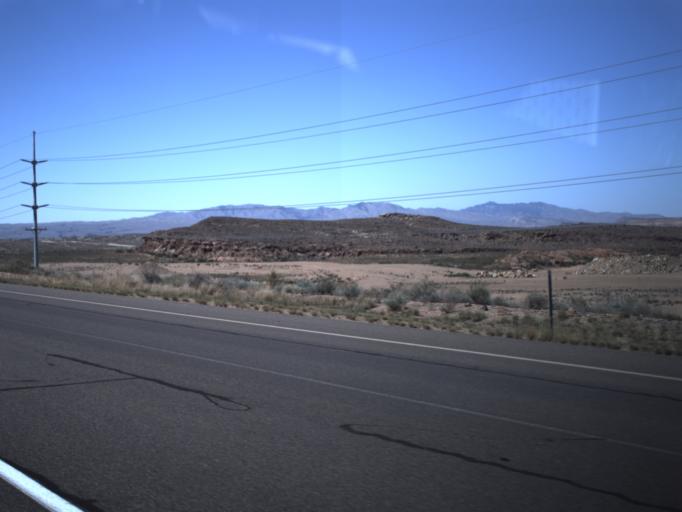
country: US
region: Utah
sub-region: Washington County
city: Saint George
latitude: 37.0072
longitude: -113.5190
